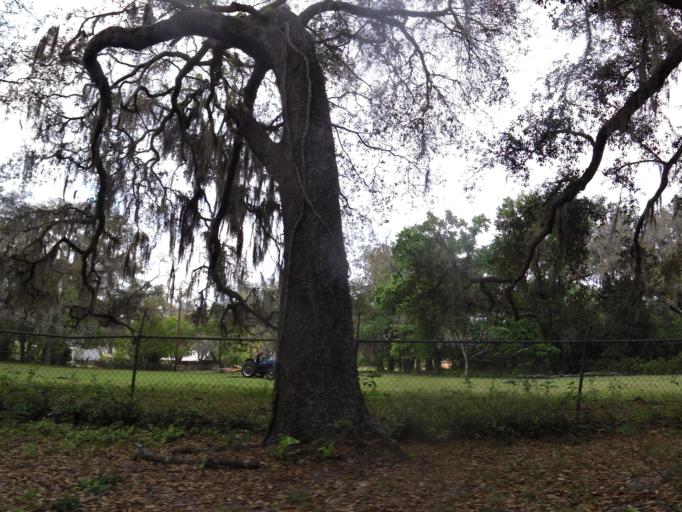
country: US
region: Georgia
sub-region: Charlton County
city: Folkston
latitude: 30.8293
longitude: -82.0159
